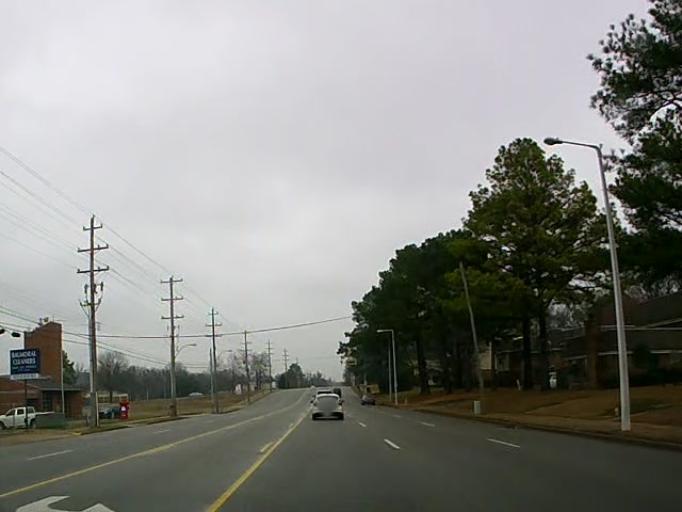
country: US
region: Tennessee
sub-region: Shelby County
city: Germantown
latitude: 35.0879
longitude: -89.8587
